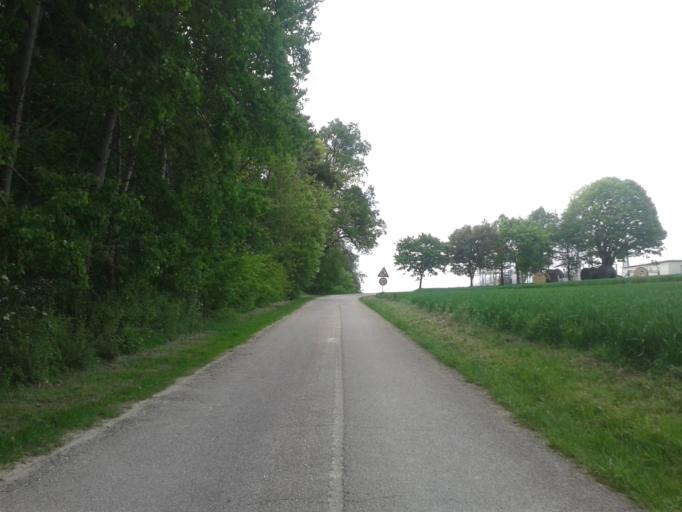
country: DE
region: Baden-Wuerttemberg
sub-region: Tuebingen Region
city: Blaubeuren
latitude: 48.3949
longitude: 9.7894
